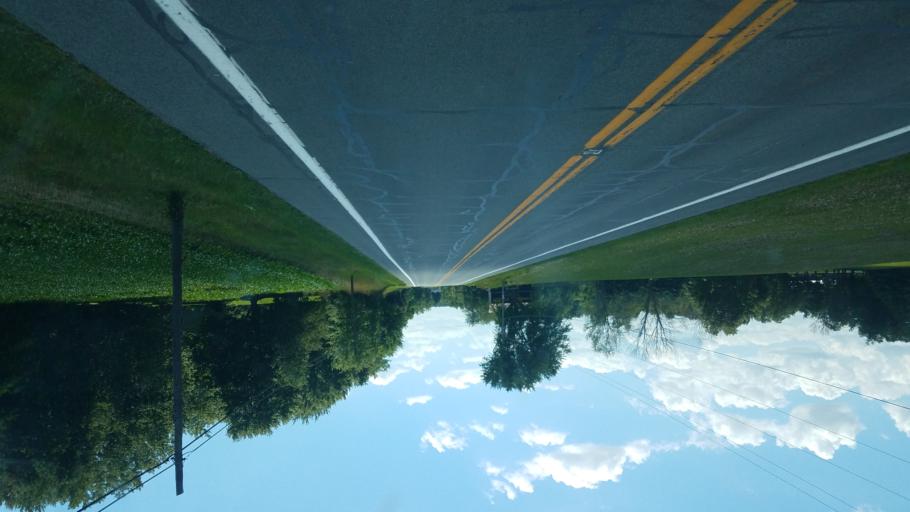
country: US
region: Ohio
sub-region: Richland County
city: Lexington
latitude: 40.6572
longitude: -82.6142
